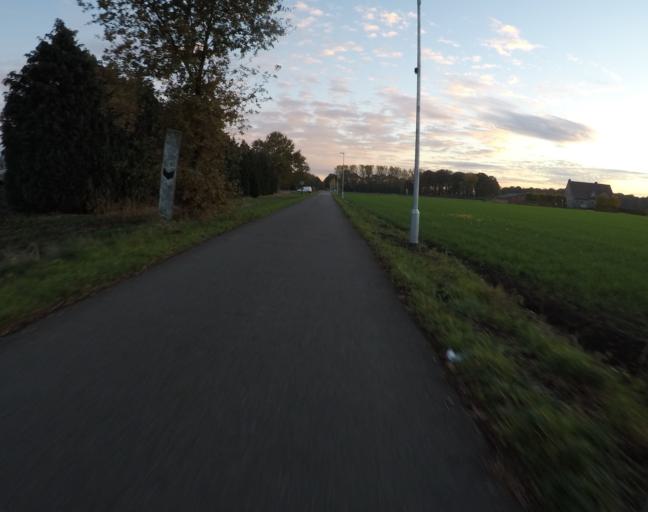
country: BE
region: Flanders
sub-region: Provincie Antwerpen
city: Olen
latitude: 51.1400
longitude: 4.8227
